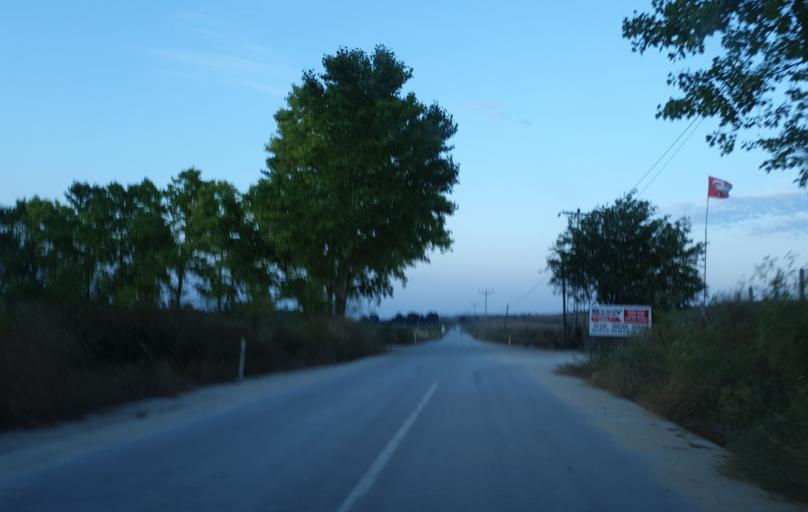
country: TR
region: Tekirdag
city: Velimese
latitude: 41.3474
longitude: 27.8683
